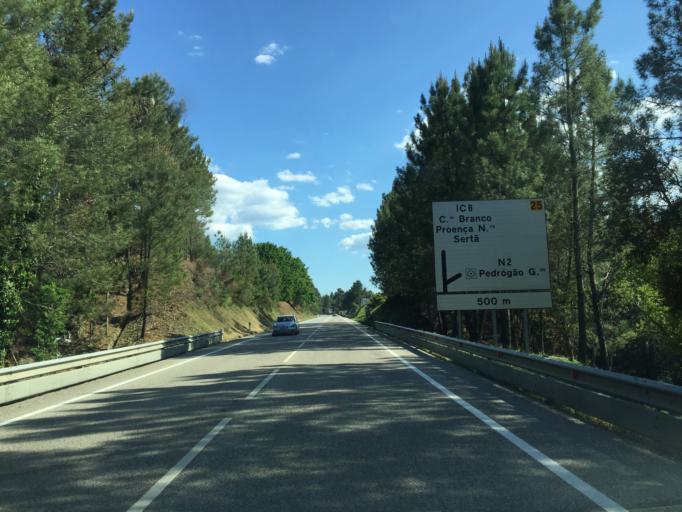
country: PT
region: Leiria
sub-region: Pedrogao Grande
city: Pedrogao Grande
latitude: 39.9162
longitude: -8.1538
